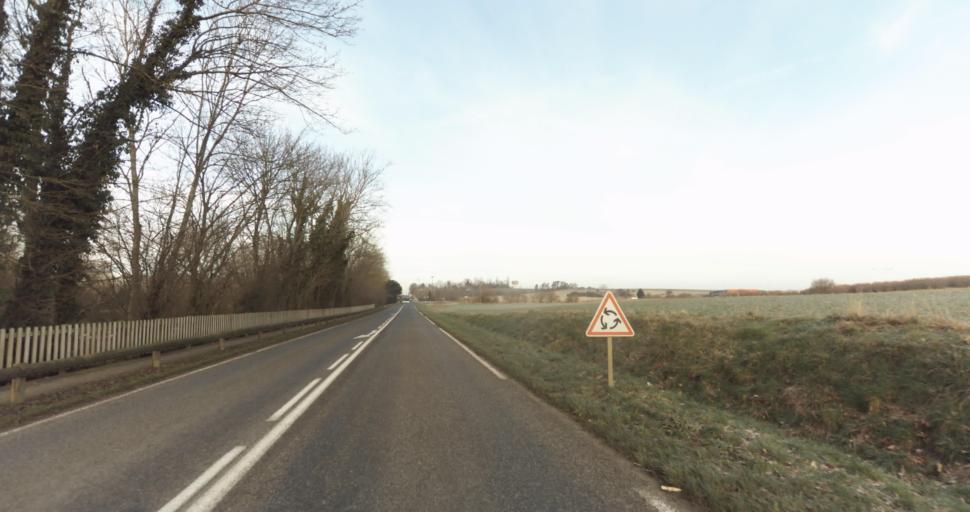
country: FR
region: Lorraine
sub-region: Departement de Meurthe-et-Moselle
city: Giraumont
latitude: 49.1508
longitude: 5.9060
